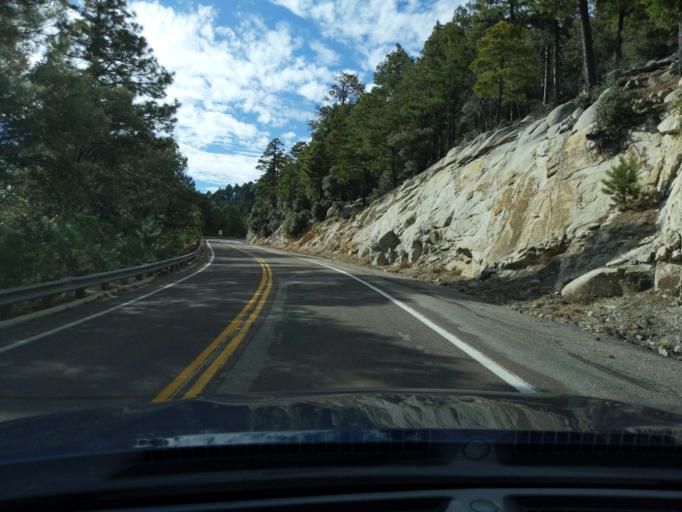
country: US
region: Arizona
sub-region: Pima County
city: Tanque Verde
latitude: 32.4108
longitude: -110.7178
